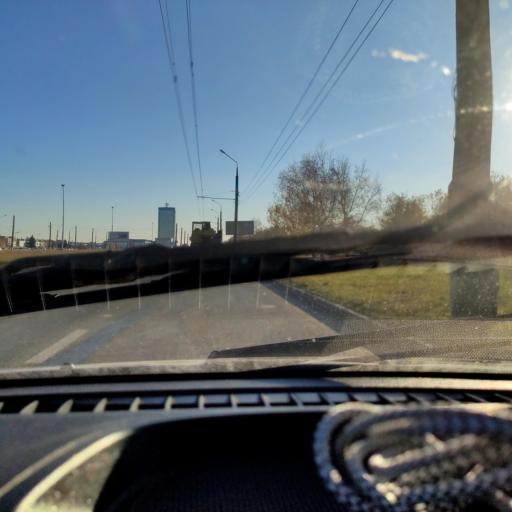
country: RU
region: Samara
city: Tol'yatti
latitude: 53.5565
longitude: 49.2468
